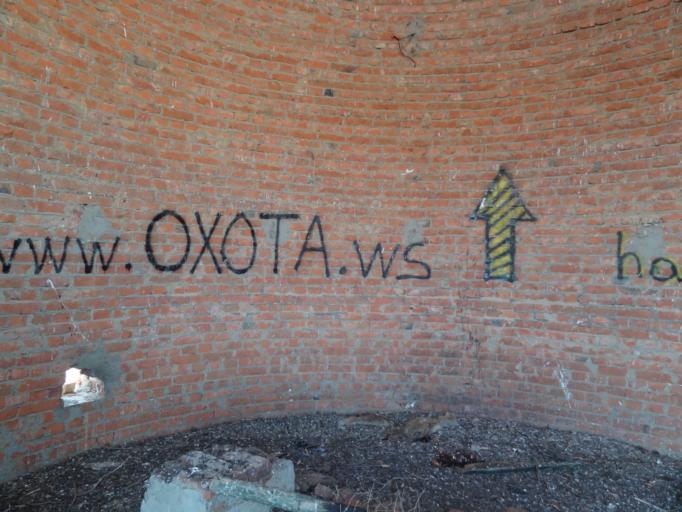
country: RU
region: Saratov
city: Shumeyka
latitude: 51.4509
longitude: 46.2577
